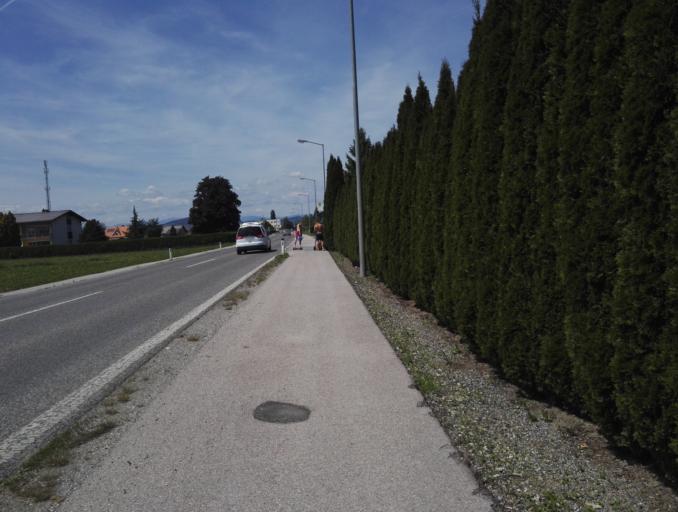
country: AT
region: Styria
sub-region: Politischer Bezirk Graz-Umgebung
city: Gossendorf
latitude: 46.9810
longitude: 15.4649
